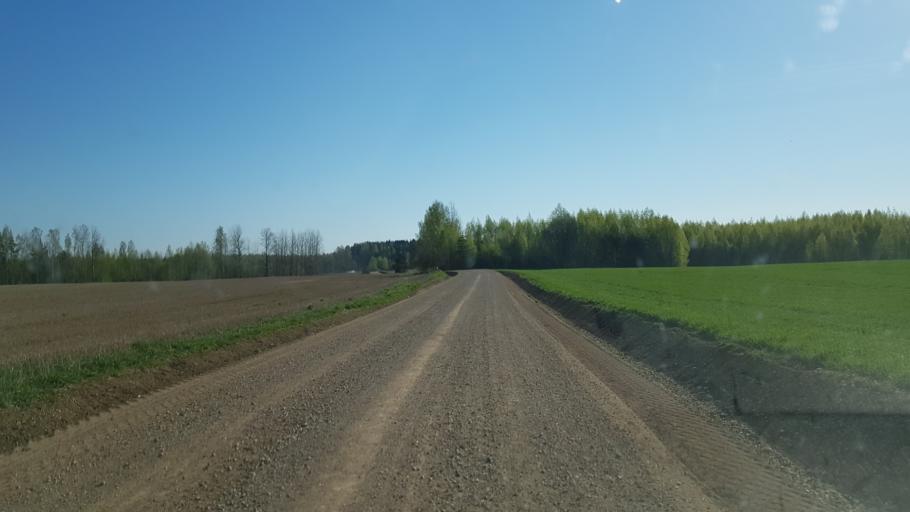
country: EE
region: Polvamaa
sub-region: Polva linn
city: Polva
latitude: 58.1041
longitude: 27.2274
